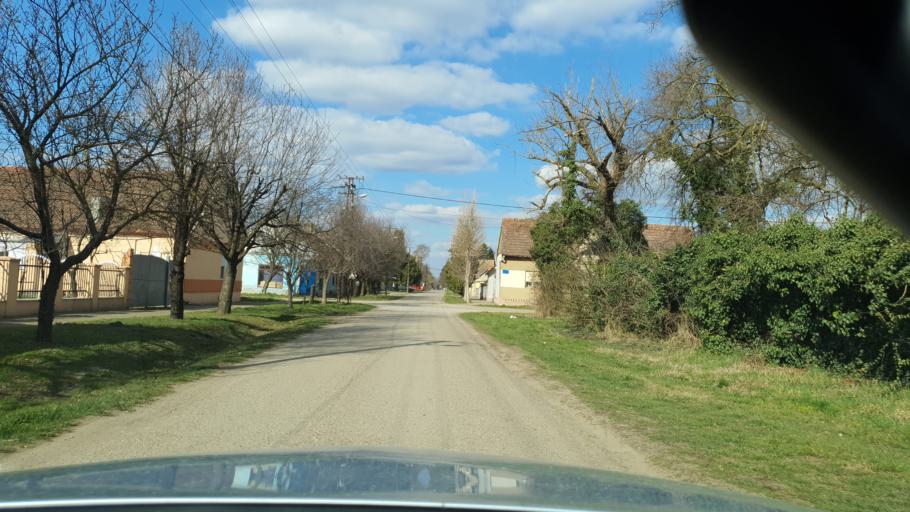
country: RS
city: Kulpin
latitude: 45.4035
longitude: 19.5860
